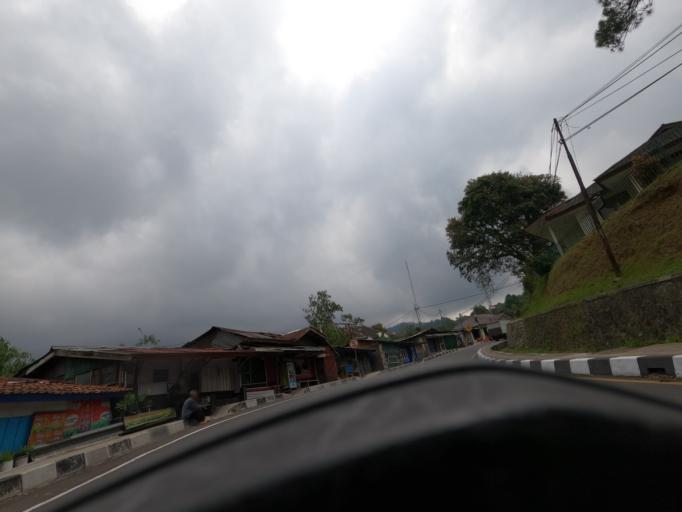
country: ID
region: West Java
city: Caringin
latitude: -6.7115
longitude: 107.0004
